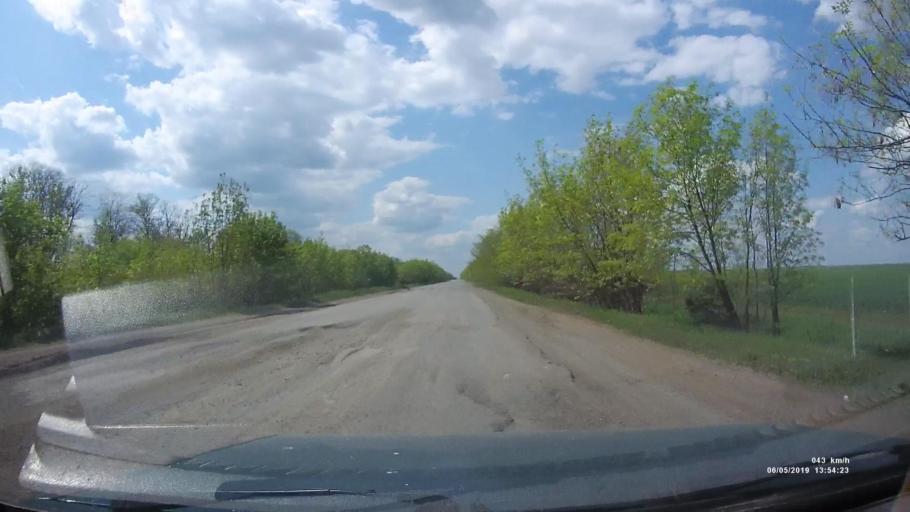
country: RU
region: Rostov
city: Melikhovskaya
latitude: 47.6740
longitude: 40.4486
